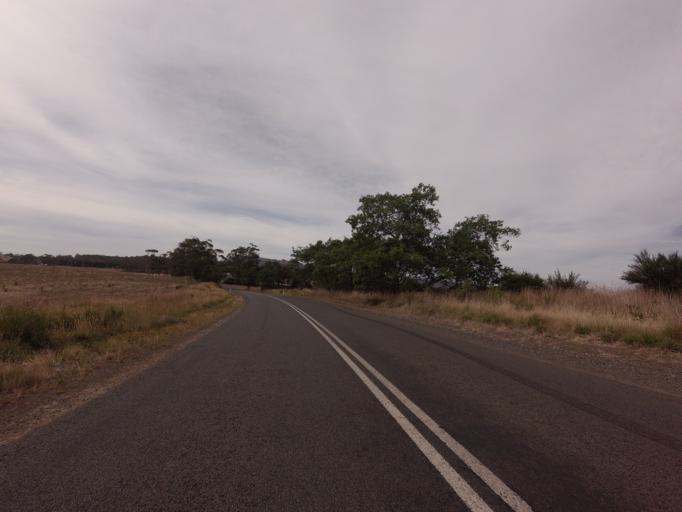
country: AU
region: Tasmania
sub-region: Sorell
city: Sorell
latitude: -42.4244
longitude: 147.4653
